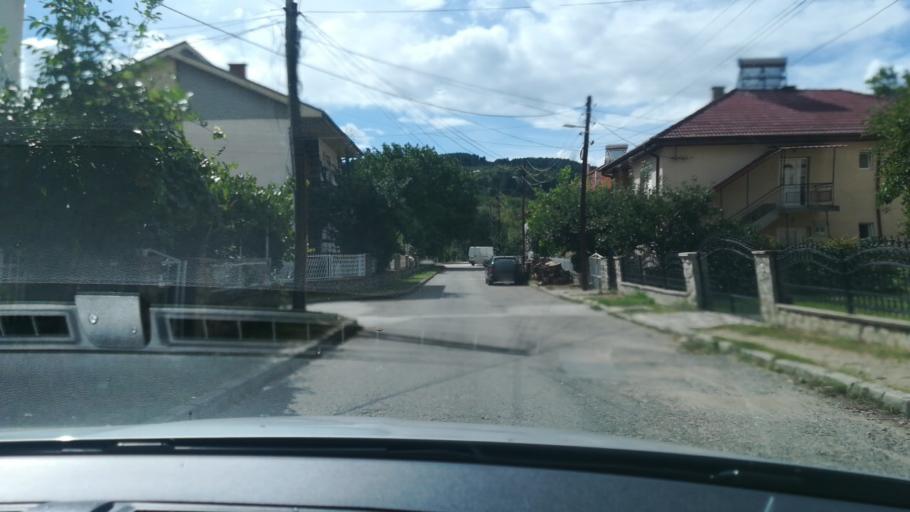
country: MK
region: Delcevo
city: Delcevo
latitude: 41.9630
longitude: 22.7788
